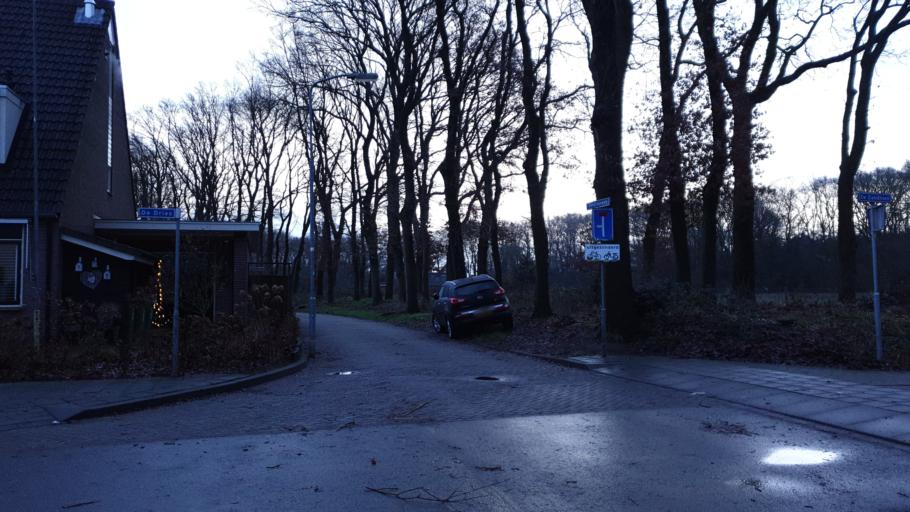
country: NL
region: Gelderland
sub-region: Gemeente Ede
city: Otterlo
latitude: 52.0996
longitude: 5.7751
